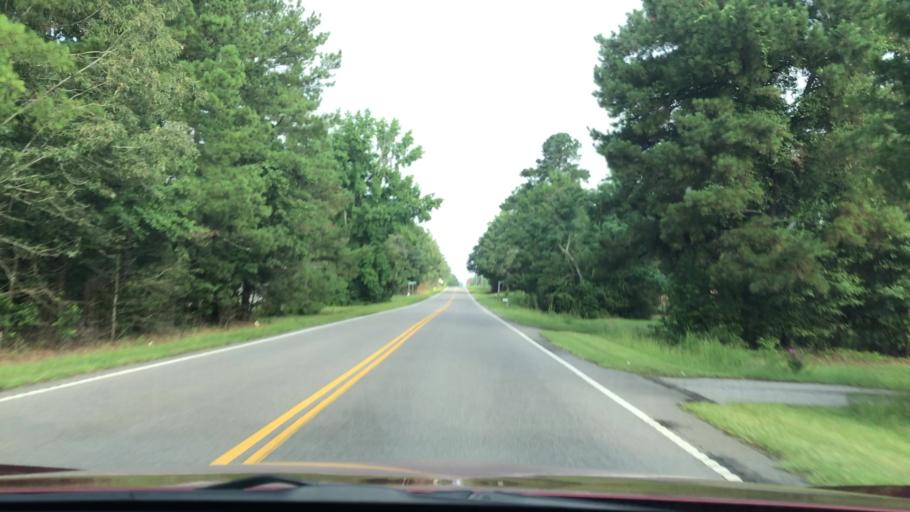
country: US
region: South Carolina
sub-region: Lexington County
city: Leesville
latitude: 33.6777
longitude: -81.4368
